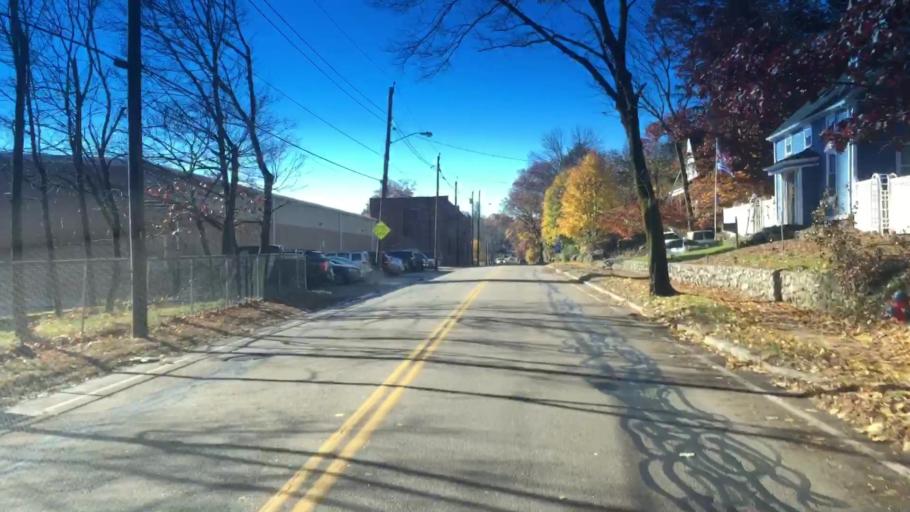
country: US
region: Massachusetts
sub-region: Norfolk County
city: Norwood
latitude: 42.1658
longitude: -71.2131
